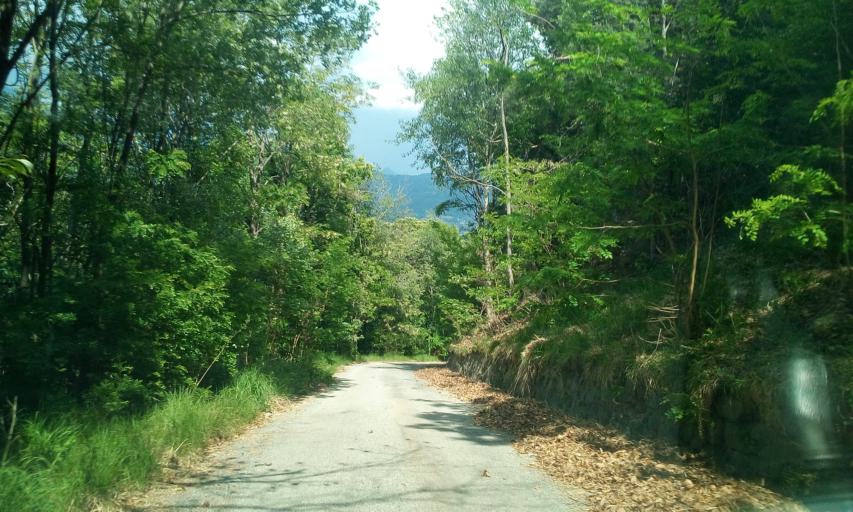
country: IT
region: Aosta Valley
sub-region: Valle d'Aosta
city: Chatillon
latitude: 45.7336
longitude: 7.6325
